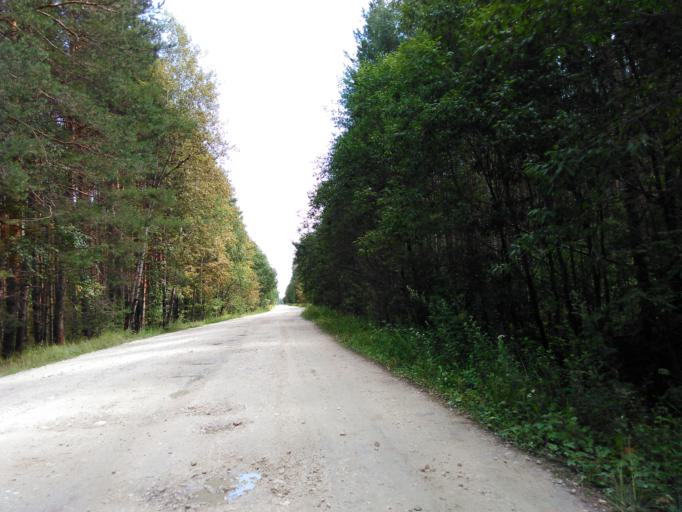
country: RU
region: Vladimir
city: Krasnyy Oktyabr'
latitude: 56.0053
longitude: 38.8357
